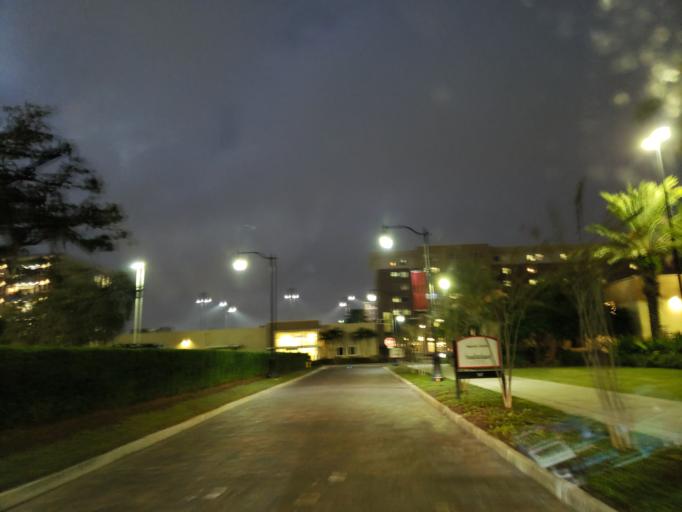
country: US
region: Florida
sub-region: Hillsborough County
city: Tampa
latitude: 27.9482
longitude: -82.4653
